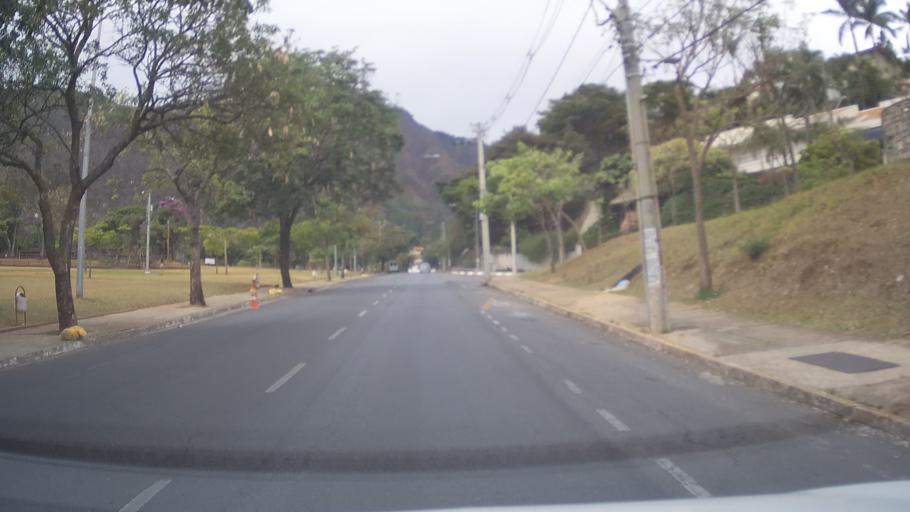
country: BR
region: Minas Gerais
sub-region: Belo Horizonte
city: Belo Horizonte
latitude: -19.9553
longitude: -43.9156
